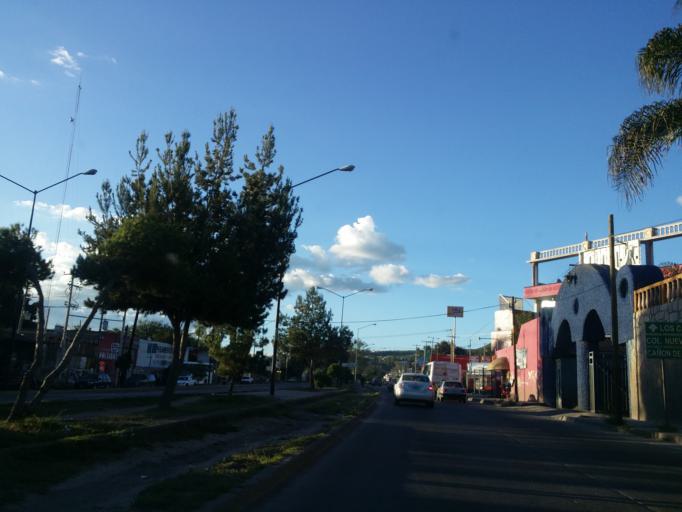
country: MX
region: Guanajuato
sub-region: Leon
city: Medina
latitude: 21.1900
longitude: -101.6644
